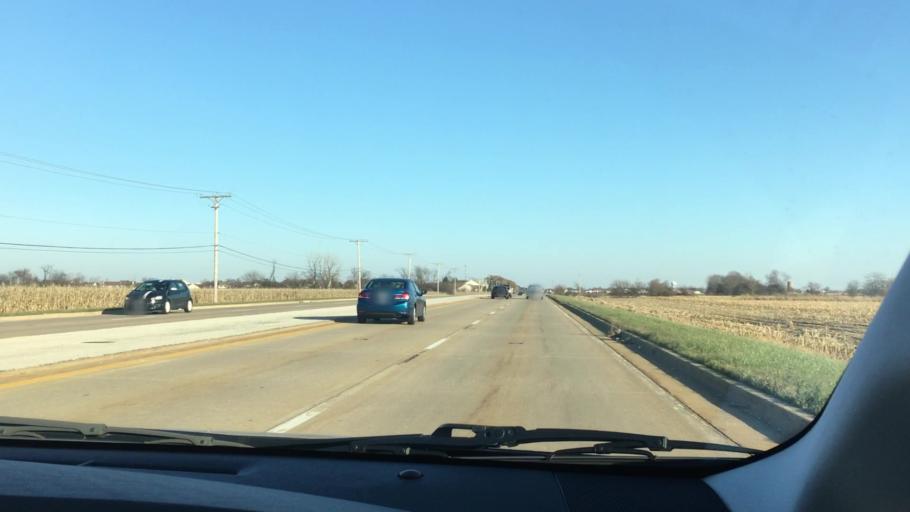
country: US
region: Illinois
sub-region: Will County
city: Frankfort Square
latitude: 41.5280
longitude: -87.7875
